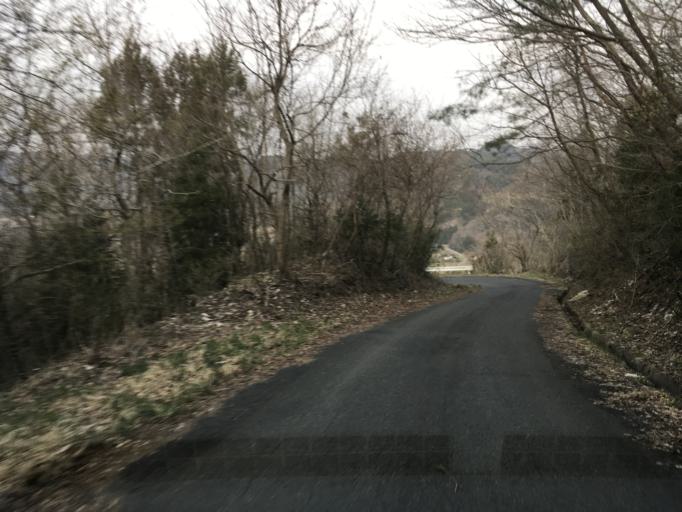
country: JP
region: Iwate
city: Ichinoseki
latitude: 38.9401
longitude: 141.2411
